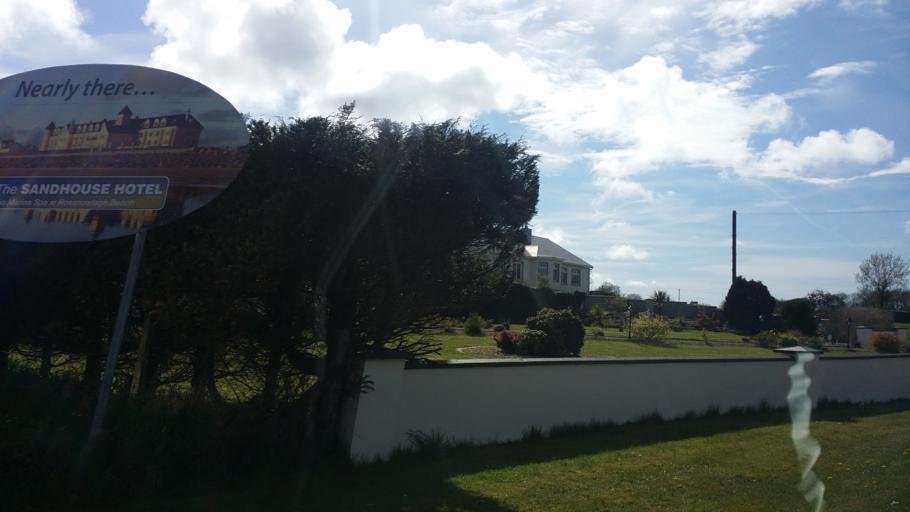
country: IE
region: Ulster
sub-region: County Donegal
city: Ballyshannon
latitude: 54.4843
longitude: -8.1242
